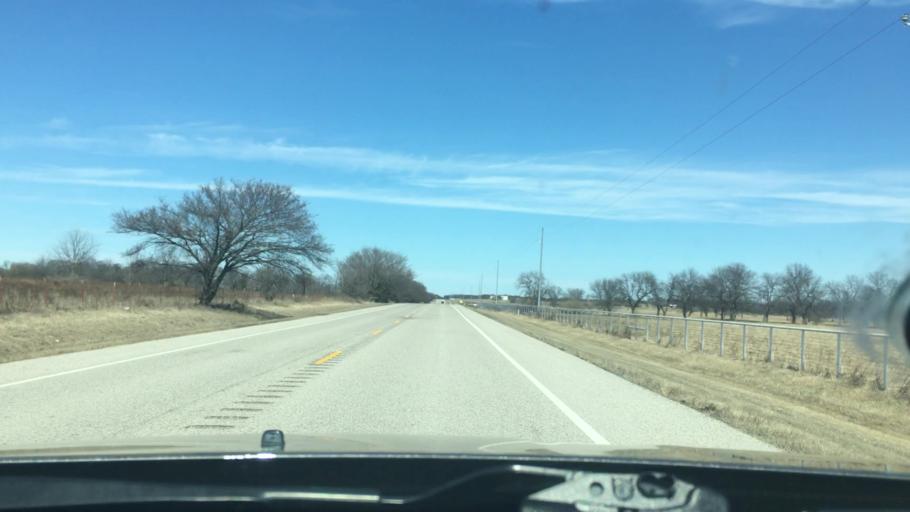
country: US
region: Oklahoma
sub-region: Murray County
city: Sulphur
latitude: 34.3675
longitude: -96.9508
